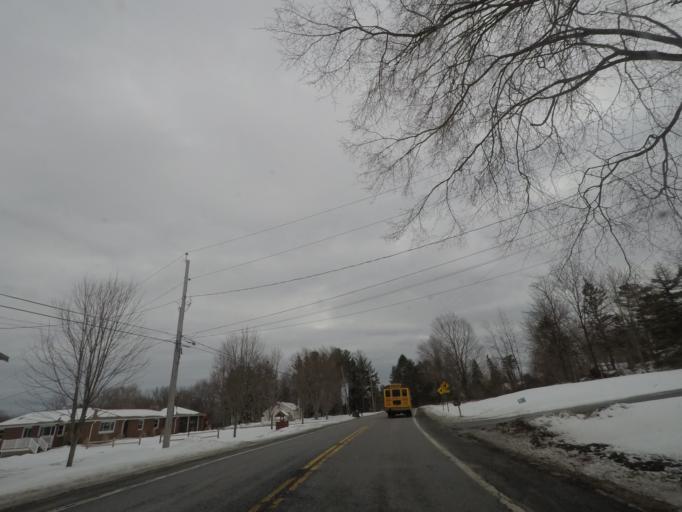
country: US
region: New York
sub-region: Saratoga County
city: Stillwater
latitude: 42.9505
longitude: -73.6654
